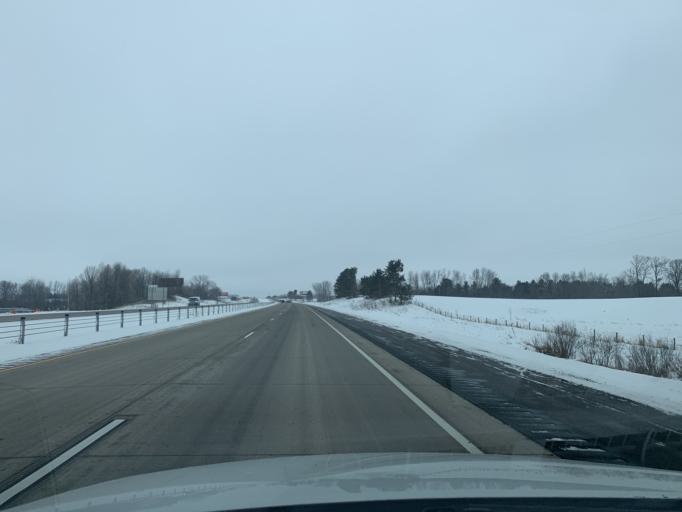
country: US
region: Minnesota
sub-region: Pine County
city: Rock Creek
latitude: 45.7512
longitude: -92.9918
